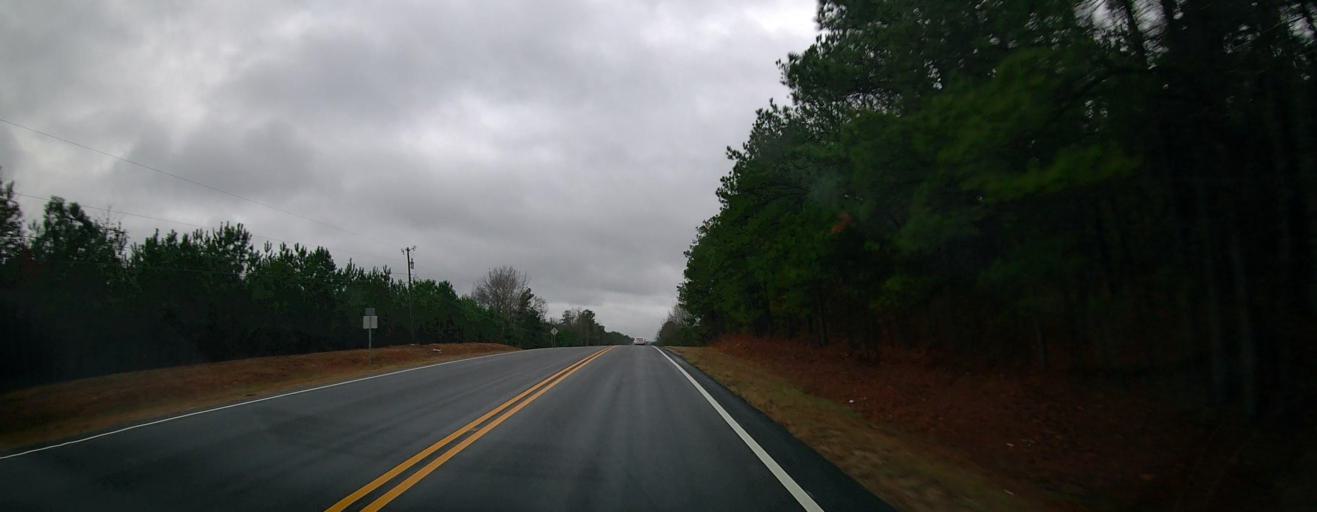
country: US
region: Alabama
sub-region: Bibb County
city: Centreville
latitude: 32.8151
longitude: -86.9344
